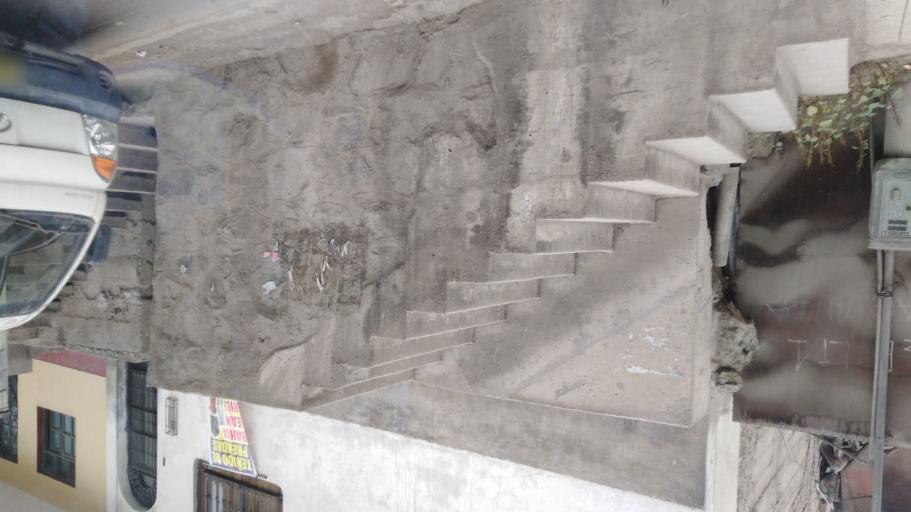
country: PE
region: Lima
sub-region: Lima
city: La Molina
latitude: -12.1456
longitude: -76.9369
